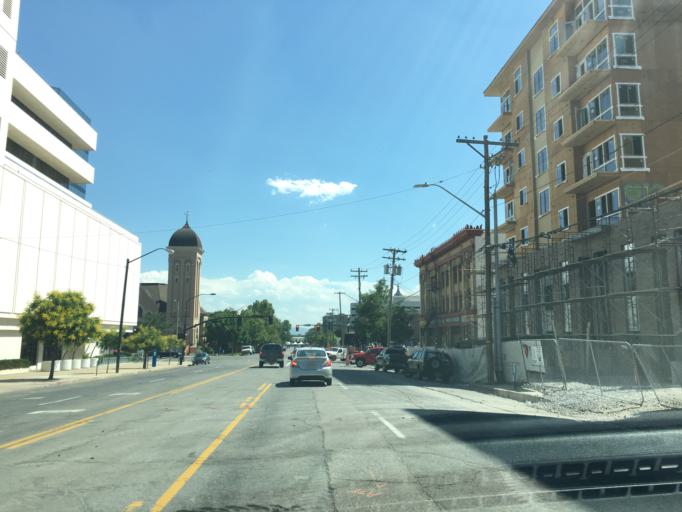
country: US
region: Utah
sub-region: Salt Lake County
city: Salt Lake City
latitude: 40.7660
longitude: -111.8854
